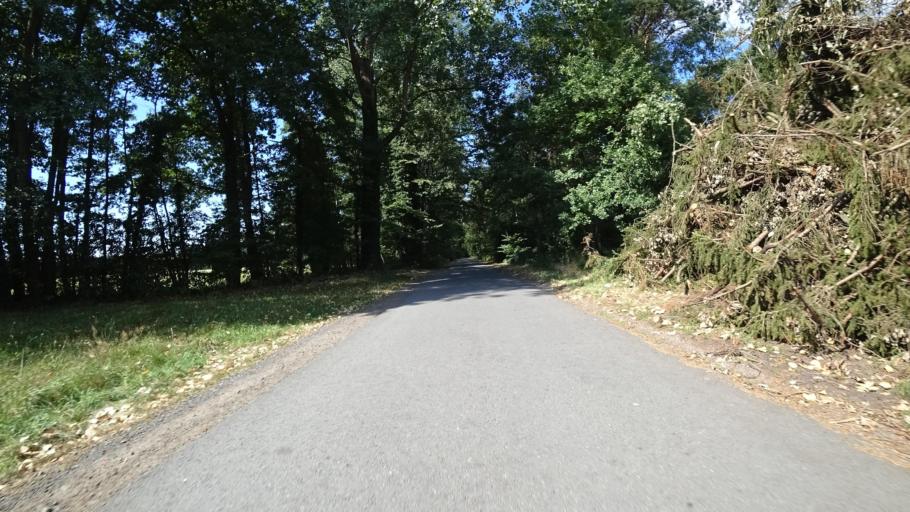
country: DE
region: North Rhine-Westphalia
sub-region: Regierungsbezirk Detmold
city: Verl
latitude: 51.9436
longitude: 8.4646
